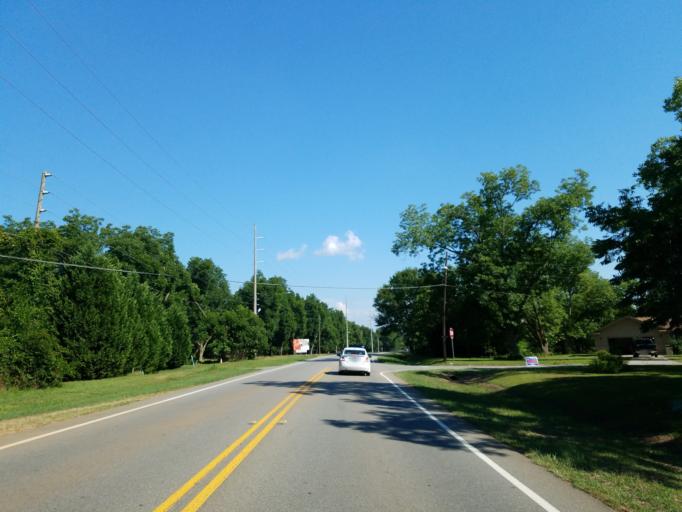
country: US
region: Georgia
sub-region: Peach County
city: Fort Valley
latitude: 32.5701
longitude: -83.8883
